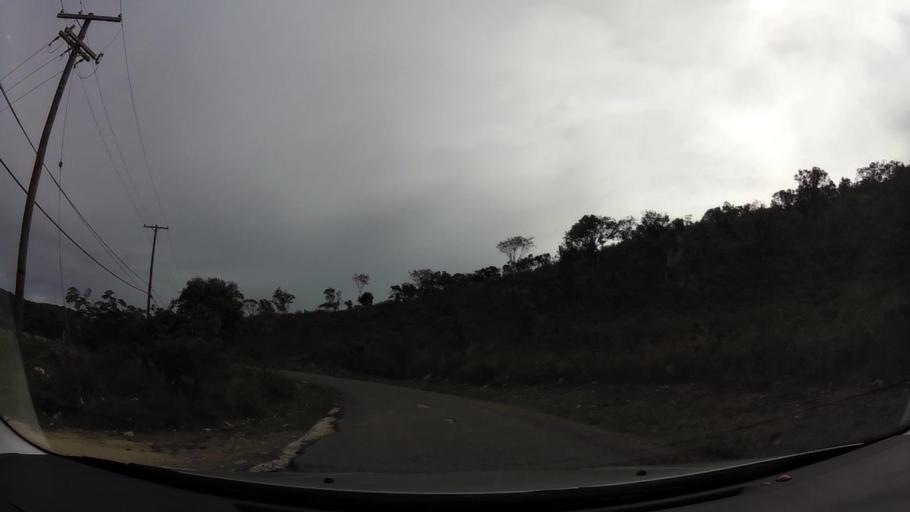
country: AG
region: Saint Peter
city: Parham
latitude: 17.0635
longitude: -61.7276
